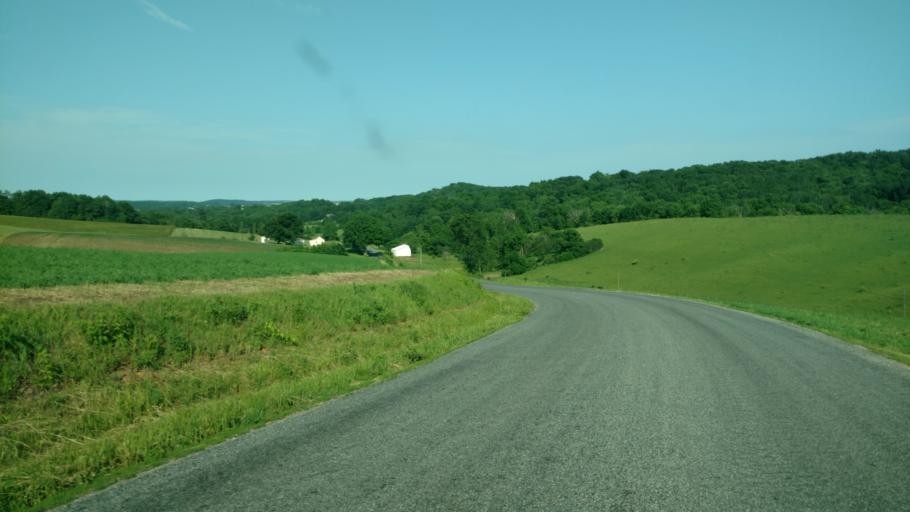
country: US
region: Wisconsin
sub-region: Vernon County
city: Hillsboro
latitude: 43.6815
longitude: -90.3678
